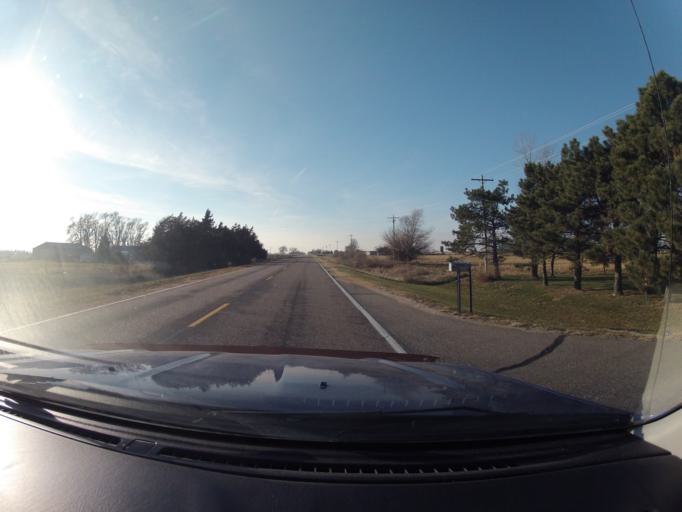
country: US
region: Nebraska
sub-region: Buffalo County
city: Kearney
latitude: 40.6410
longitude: -98.9653
